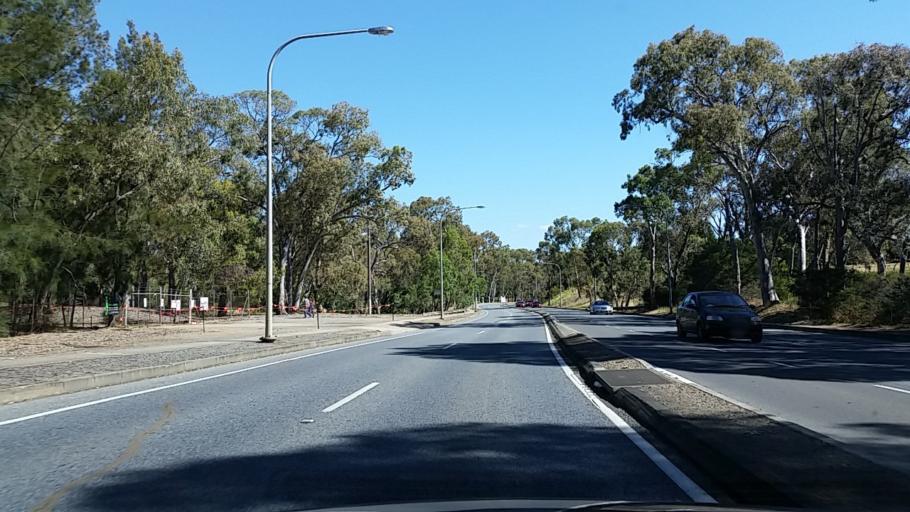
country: AU
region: South Australia
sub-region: Tea Tree Gully
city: Hope Valley
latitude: -34.8181
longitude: 138.6951
